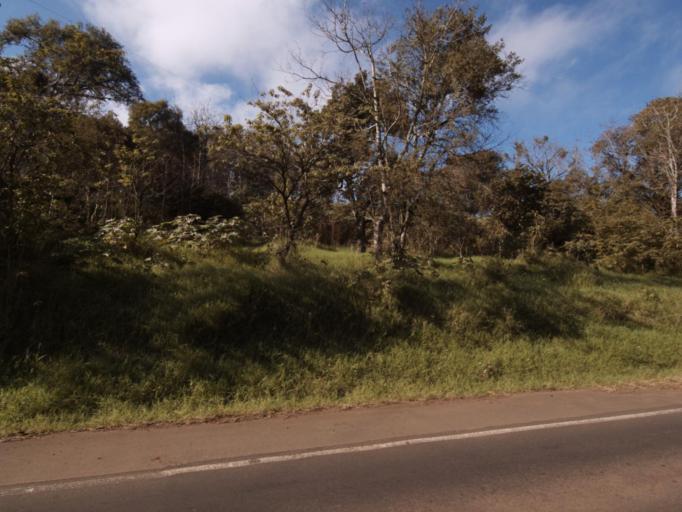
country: BR
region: Rio Grande do Sul
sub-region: Frederico Westphalen
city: Frederico Westphalen
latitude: -27.0714
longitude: -53.2315
